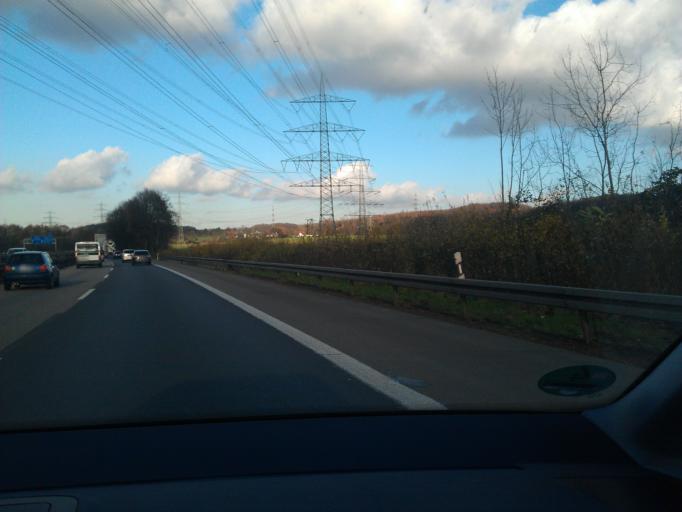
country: DE
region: North Rhine-Westphalia
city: Witten
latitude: 51.4400
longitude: 7.2929
